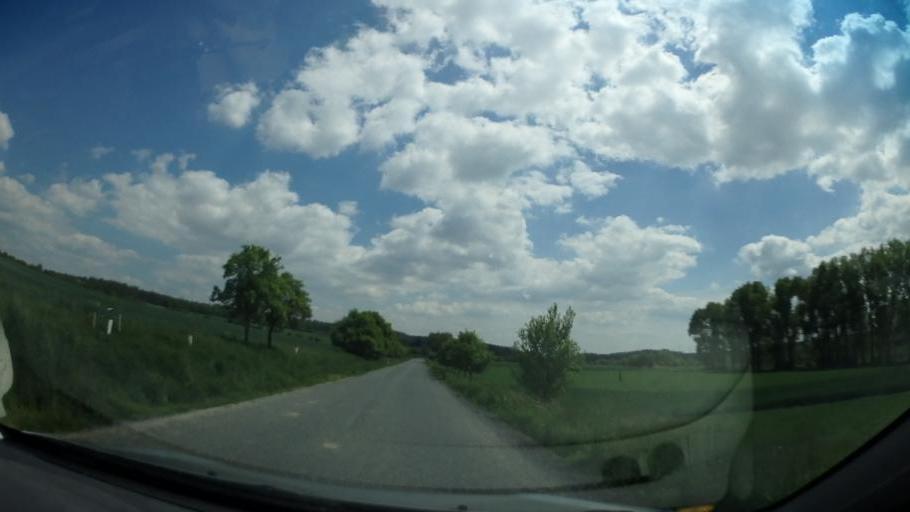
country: CZ
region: Vysocina
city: Hrotovice
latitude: 49.1278
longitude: 16.0851
